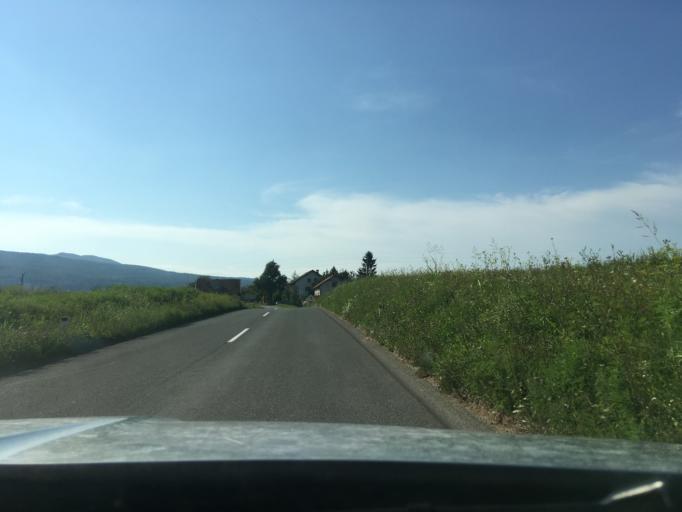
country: SI
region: Crnomelj
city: Crnomelj
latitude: 45.5177
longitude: 15.1786
